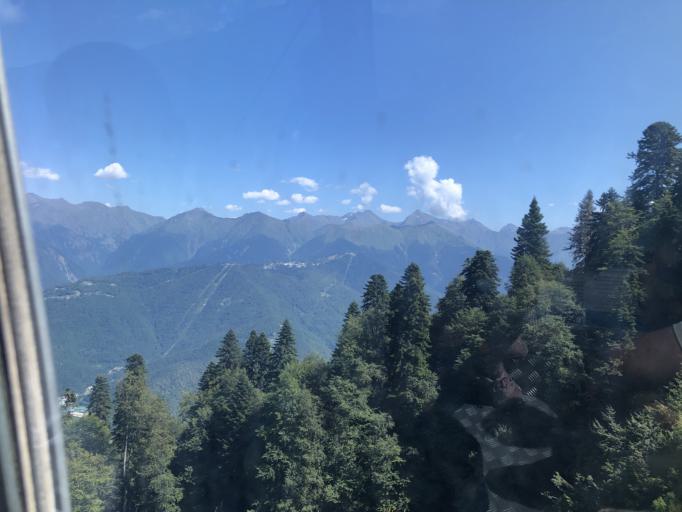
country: RU
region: Krasnodarskiy
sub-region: Sochi City
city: Krasnaya Polyana
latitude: 43.6579
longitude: 40.2516
